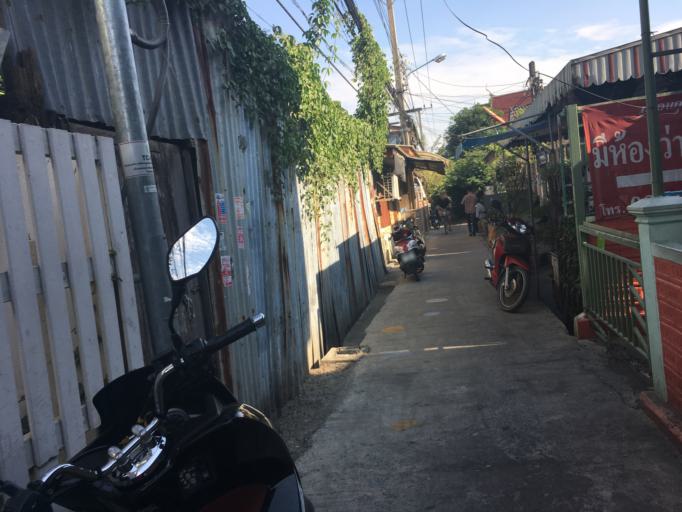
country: TH
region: Bangkok
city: Bangkok Yai
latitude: 13.7316
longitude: 100.4627
